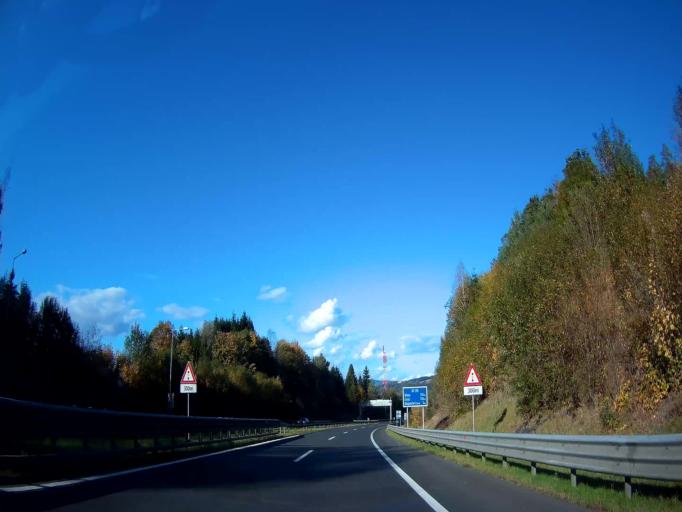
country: AT
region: Carinthia
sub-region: Klagenfurt am Woerthersee
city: Klagenfurt am Woerthersee
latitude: 46.6452
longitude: 14.2524
